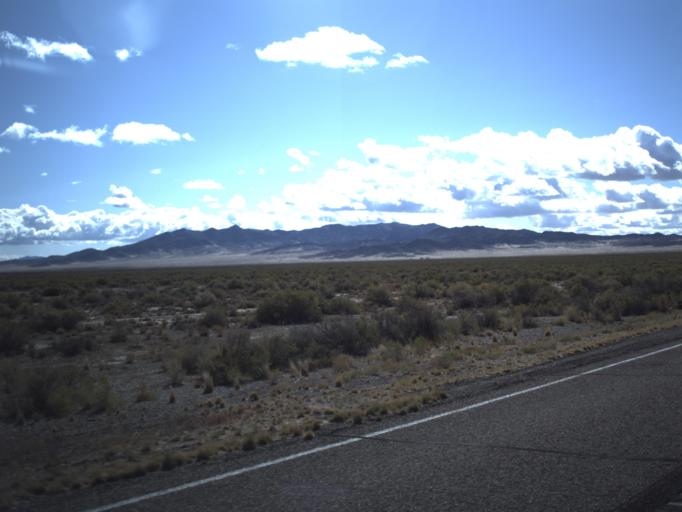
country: US
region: Nevada
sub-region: White Pine County
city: McGill
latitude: 39.0339
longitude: -114.0359
